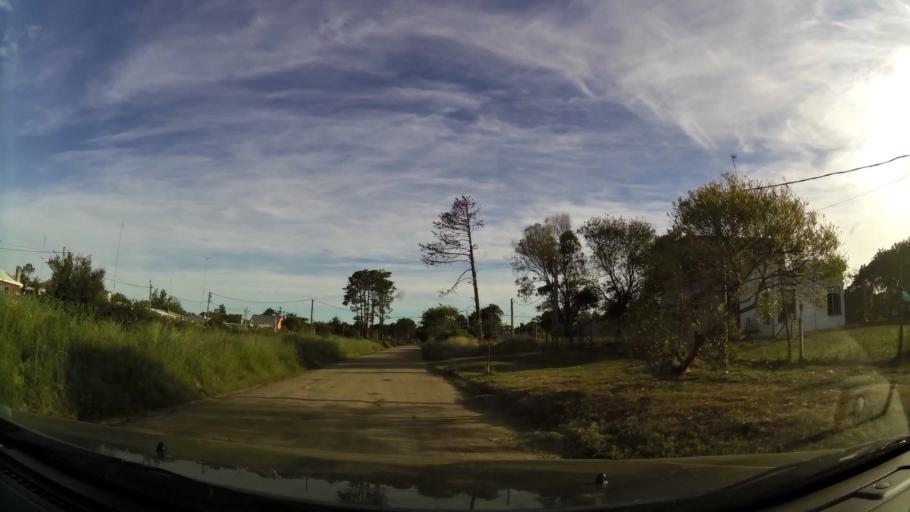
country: UY
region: Canelones
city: Empalme Olmos
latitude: -34.7742
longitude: -55.8641
